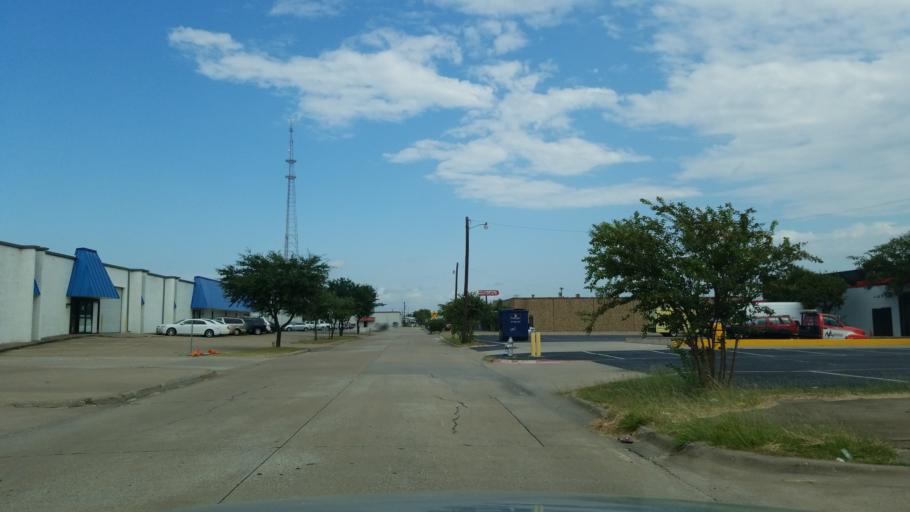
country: US
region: Texas
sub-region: Dallas County
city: Garland
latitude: 32.8951
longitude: -96.6860
